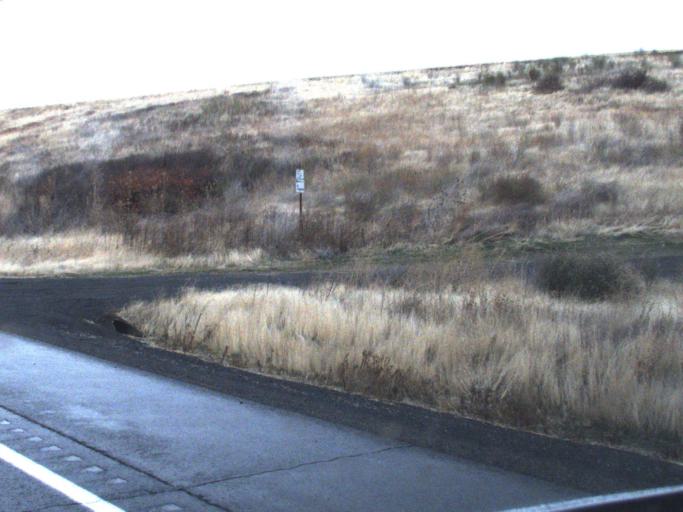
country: US
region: Washington
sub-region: Whitman County
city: Colfax
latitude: 46.8358
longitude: -117.3358
